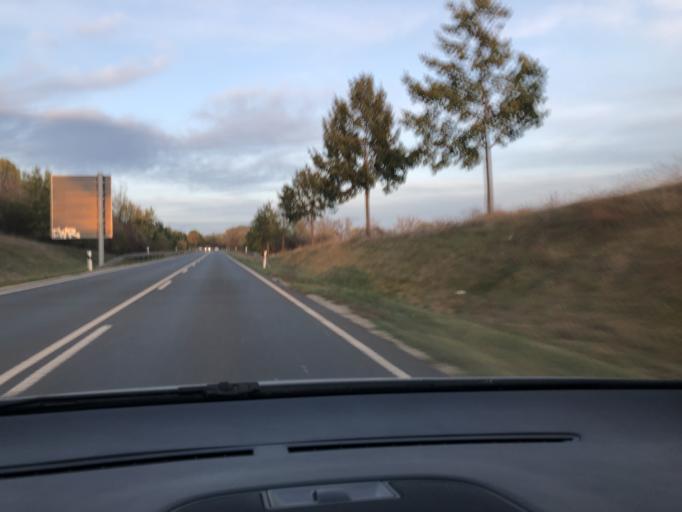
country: DE
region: Thuringia
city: Hopfgarten
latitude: 50.9949
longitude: 11.2918
